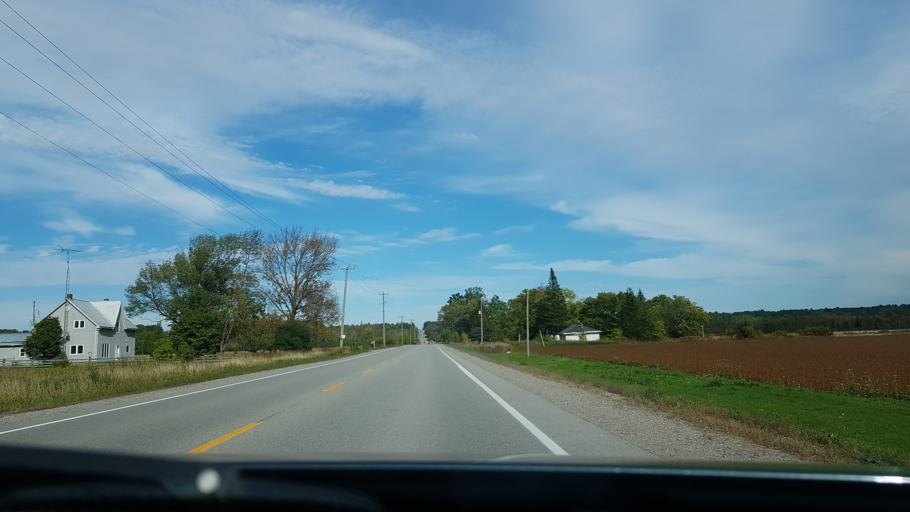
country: CA
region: Ontario
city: Angus
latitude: 44.4764
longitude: -79.8427
